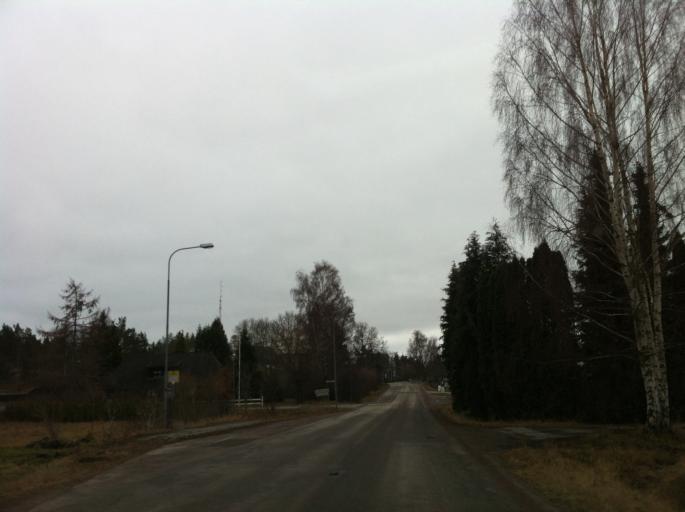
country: SE
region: Kalmar
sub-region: Vasterviks Kommun
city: Vaestervik
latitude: 57.8062
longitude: 16.5947
